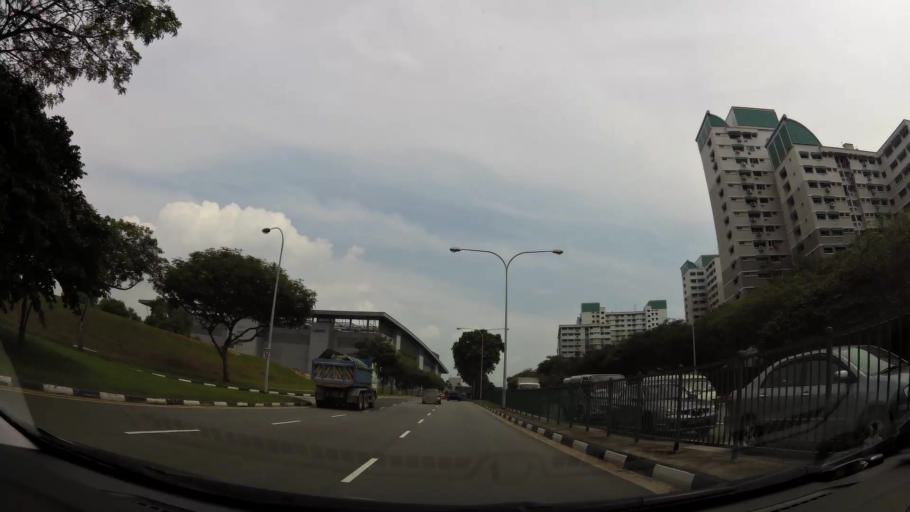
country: MY
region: Johor
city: Kampung Pasir Gudang Baru
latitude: 1.3762
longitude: 103.9320
